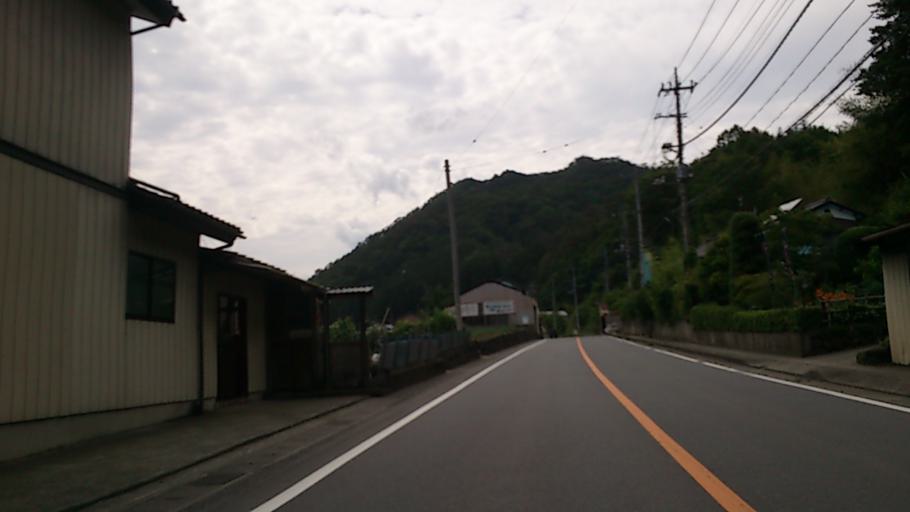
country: JP
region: Gunma
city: Tomioka
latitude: 36.2302
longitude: 138.7579
